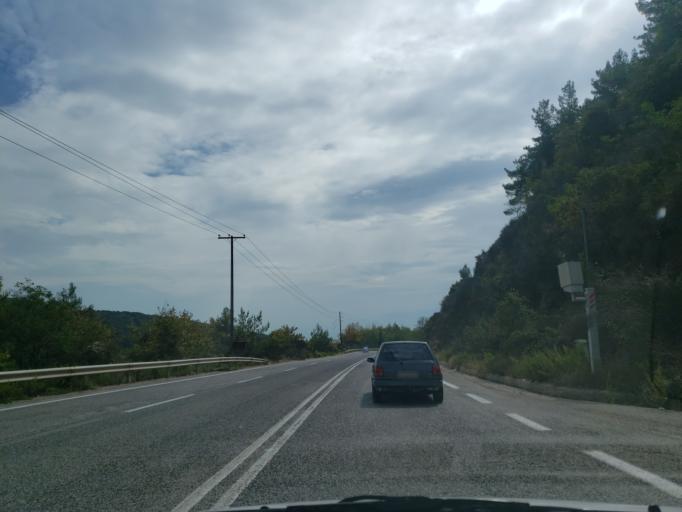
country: GR
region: Central Greece
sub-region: Nomos Fthiotidos
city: Stavros
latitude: 38.9865
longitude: 22.3785
